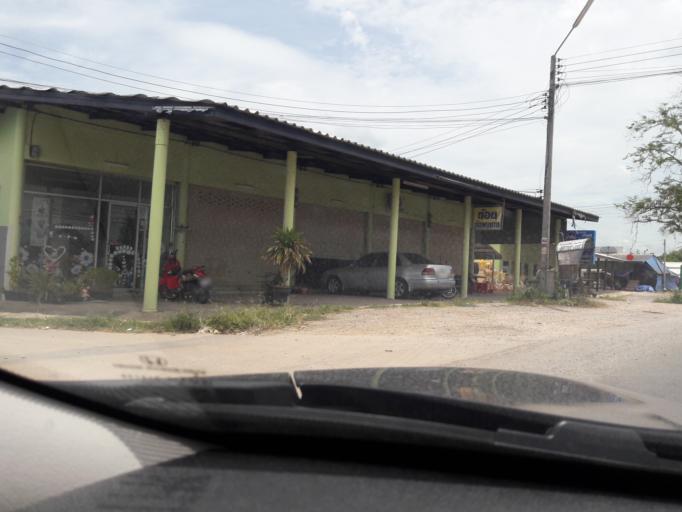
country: TH
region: Ratchaburi
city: Damnoen Saduak
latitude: 13.5919
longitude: 99.9507
